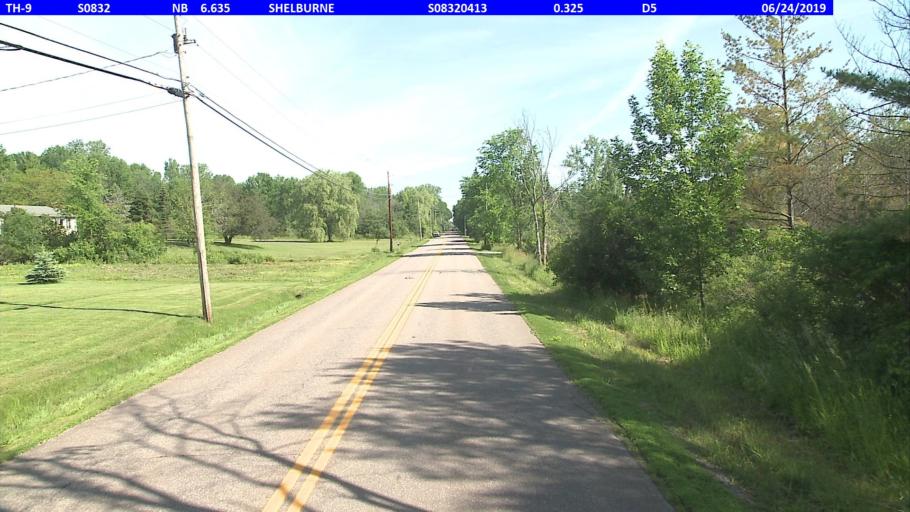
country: US
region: Vermont
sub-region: Chittenden County
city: Hinesburg
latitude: 44.3601
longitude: -73.2220
